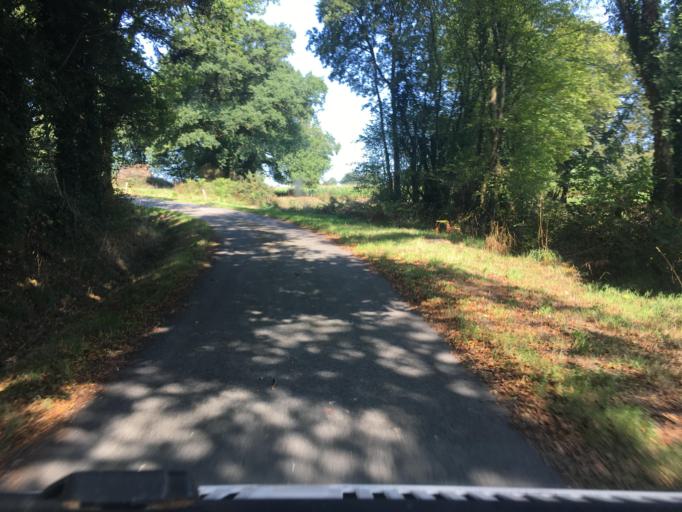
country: FR
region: Brittany
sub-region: Departement des Cotes-d'Armor
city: Mur-de-Bretagne
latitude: 48.2240
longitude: -3.0152
